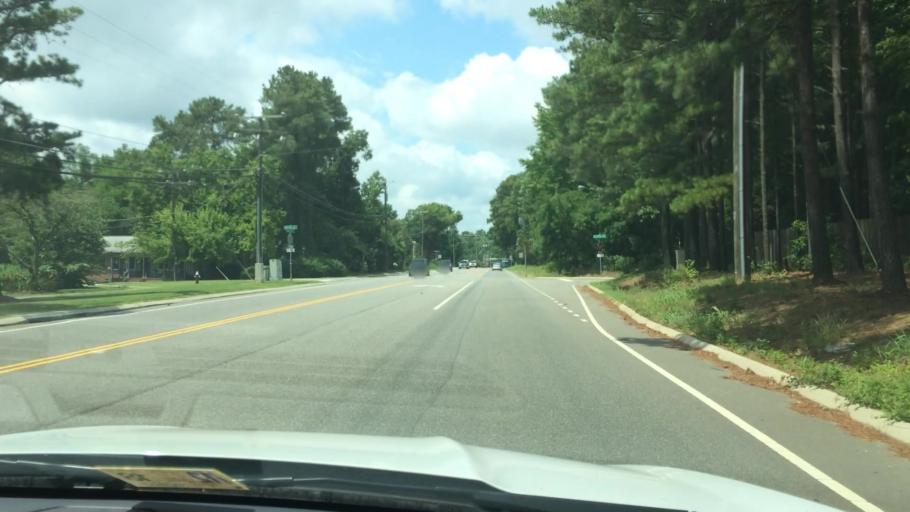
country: US
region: Virginia
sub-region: York County
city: Yorktown
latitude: 37.1492
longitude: -76.4543
